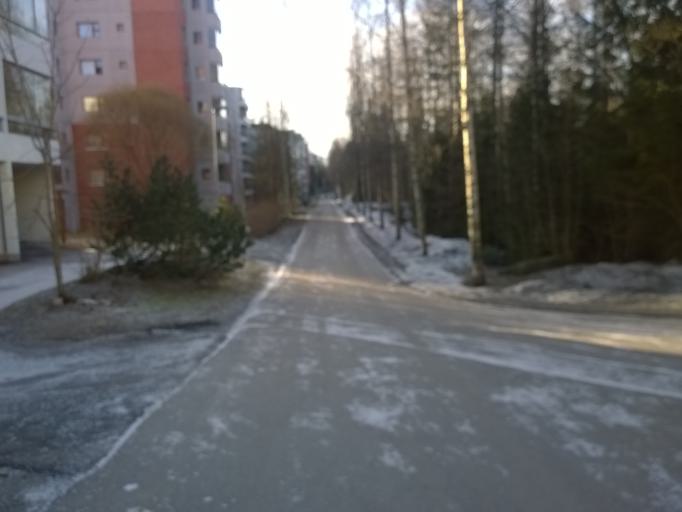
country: FI
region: Pirkanmaa
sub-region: Tampere
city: Tampere
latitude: 61.4444
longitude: 23.8540
